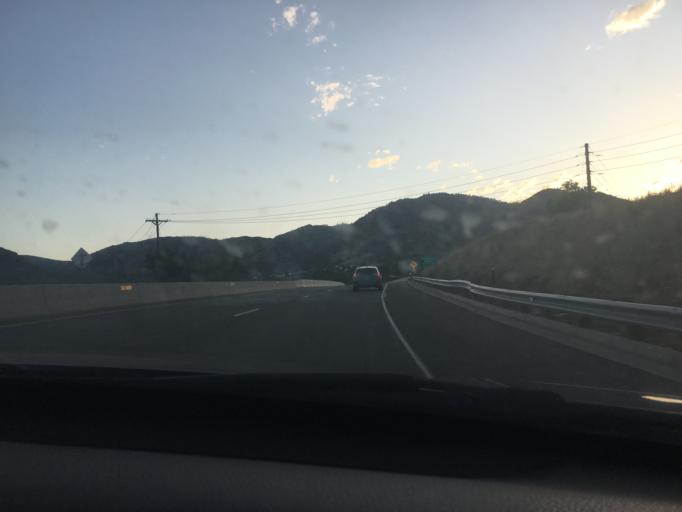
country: US
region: Colorado
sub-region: Jefferson County
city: Golden
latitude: 39.7617
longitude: -105.2204
